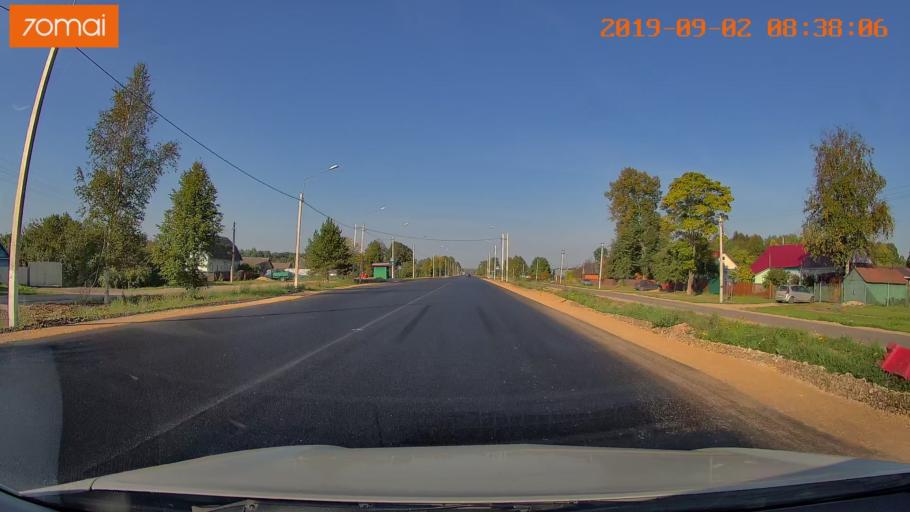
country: RU
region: Kaluga
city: Kudinovo
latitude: 54.9783
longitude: 36.1857
